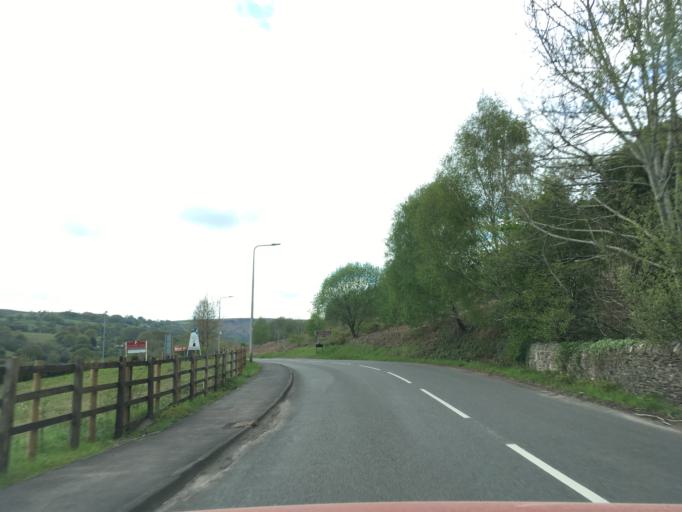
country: GB
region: Wales
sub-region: Merthyr Tydfil County Borough
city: Treharris
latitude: 51.6895
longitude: -3.2992
